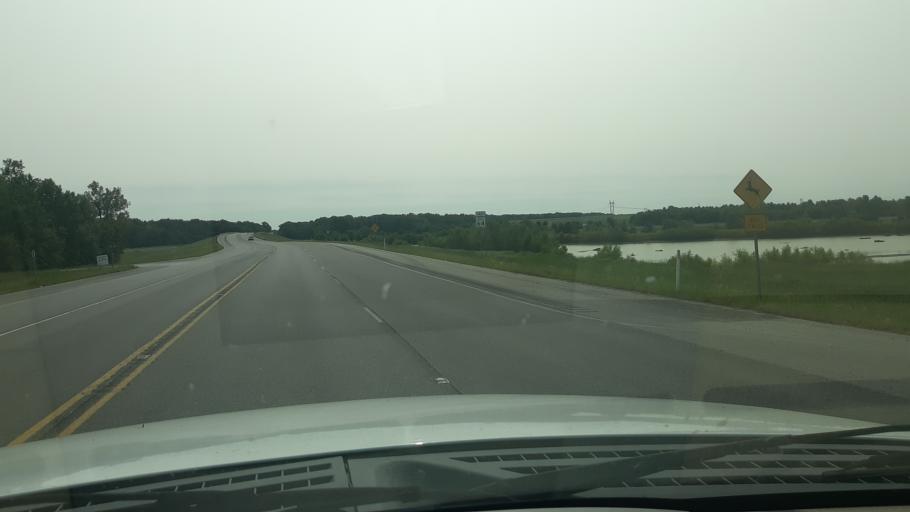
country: US
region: Illinois
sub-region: Wabash County
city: Mount Carmel
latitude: 38.3926
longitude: -87.7455
